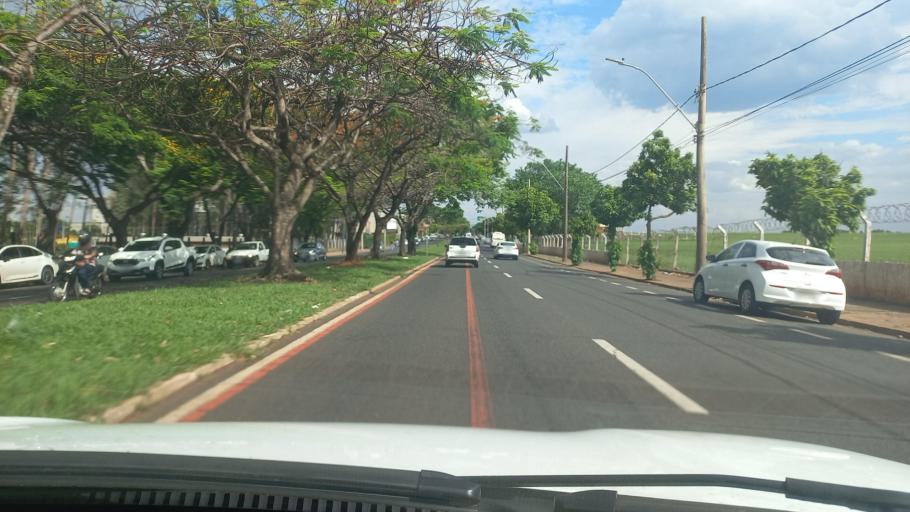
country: BR
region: Minas Gerais
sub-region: Uberaba
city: Uberaba
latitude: -19.7623
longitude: -47.9635
